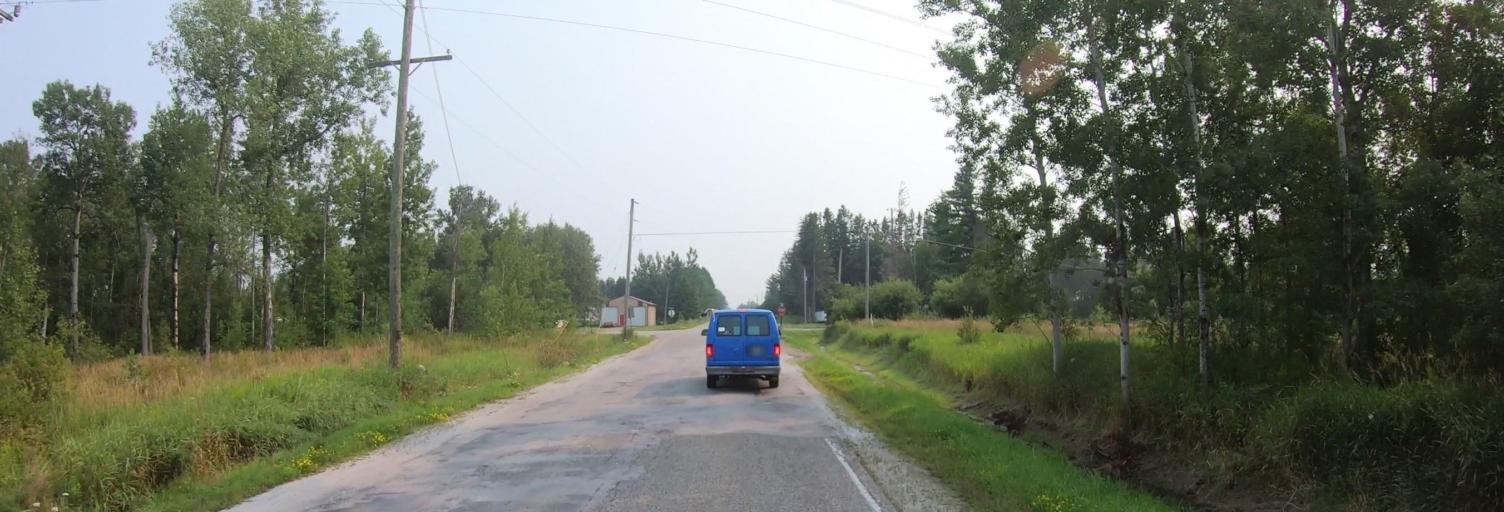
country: US
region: Michigan
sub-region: Chippewa County
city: Sault Ste. Marie
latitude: 46.4635
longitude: -84.3013
